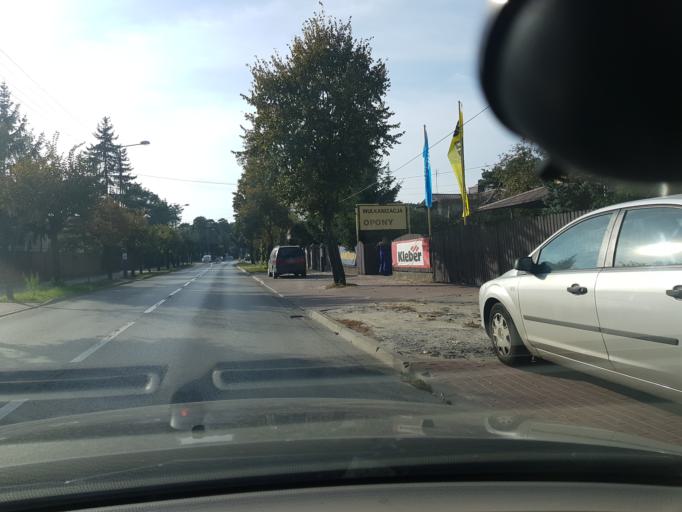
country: PL
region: Masovian Voivodeship
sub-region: Powiat otwocki
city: Otwock
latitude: 52.1063
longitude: 21.2409
